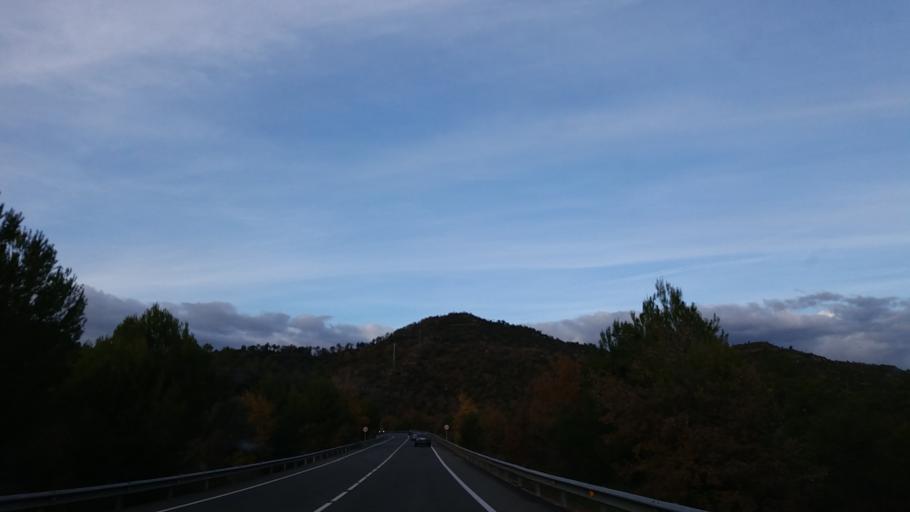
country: ES
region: Catalonia
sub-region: Provincia de Lleida
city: Tiurana
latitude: 41.9815
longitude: 1.2933
